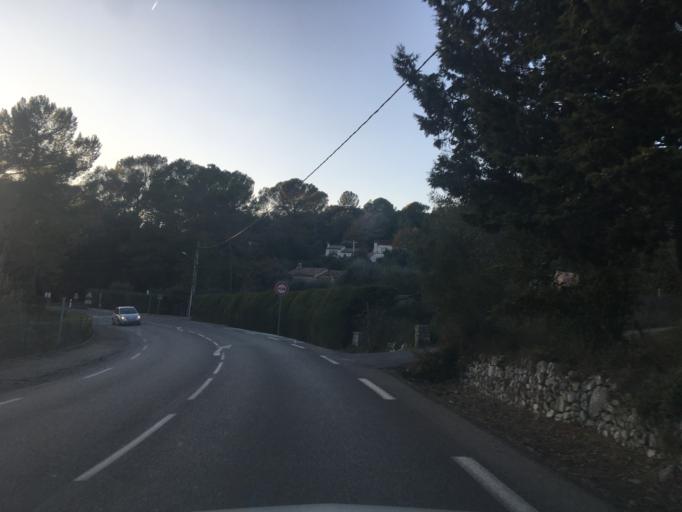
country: FR
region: Provence-Alpes-Cote d'Azur
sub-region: Departement des Alpes-Maritimes
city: Le Tignet
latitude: 43.6330
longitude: 6.8465
